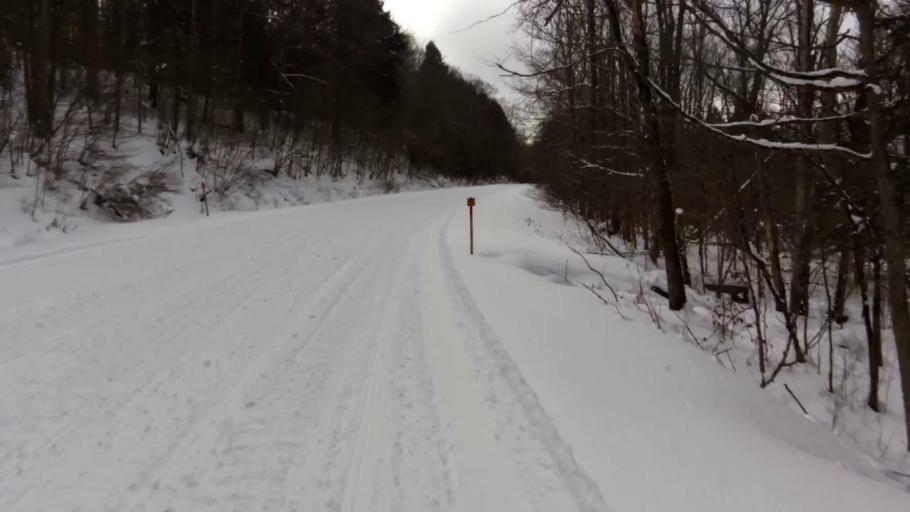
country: US
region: New York
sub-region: Cattaraugus County
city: Salamanca
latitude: 42.0761
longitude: -78.7518
